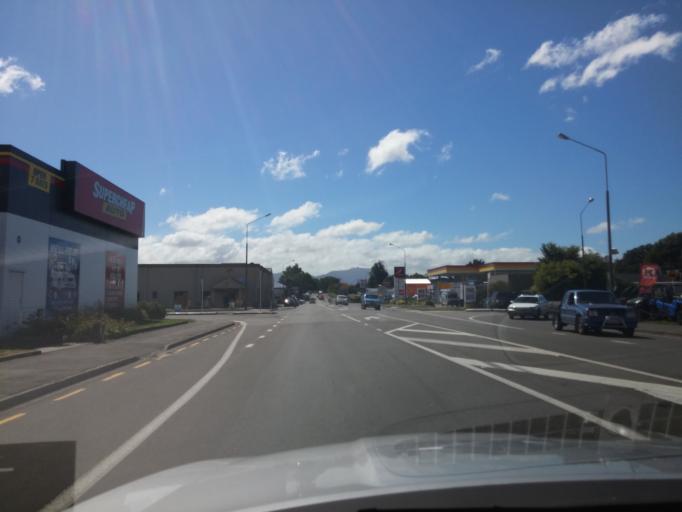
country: NZ
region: Marlborough
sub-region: Marlborough District
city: Blenheim
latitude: -41.5038
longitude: 173.9604
